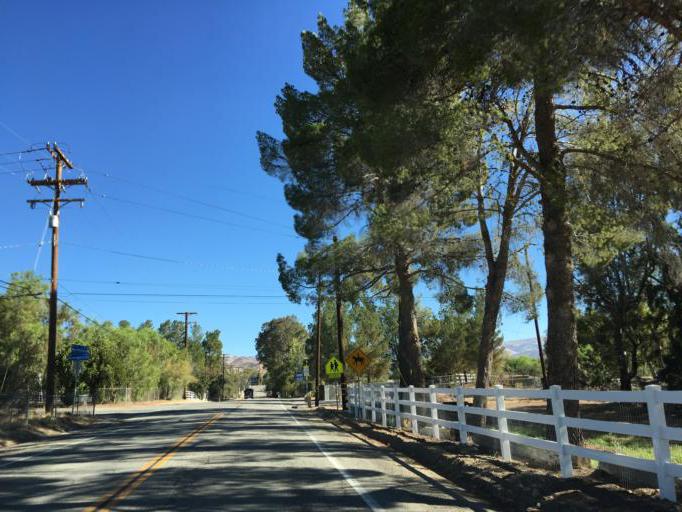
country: US
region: California
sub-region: Los Angeles County
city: Agua Dulce
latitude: 34.4851
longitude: -118.3308
